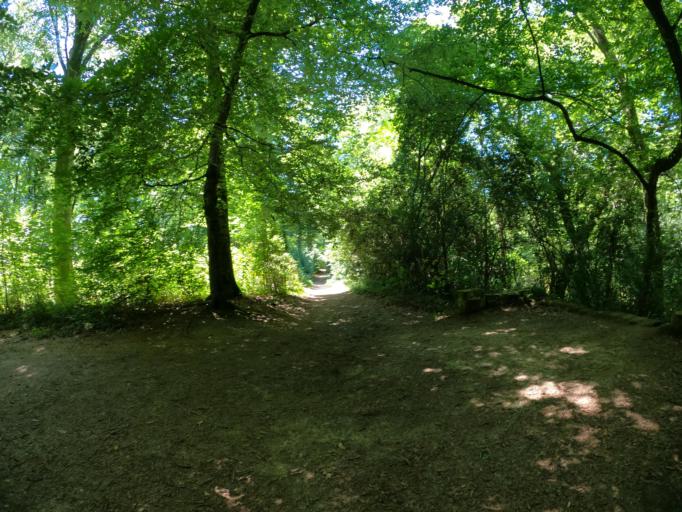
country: FR
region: Aquitaine
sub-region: Departement des Pyrenees-Atlantiques
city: Boucau
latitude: 43.5284
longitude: -1.4518
